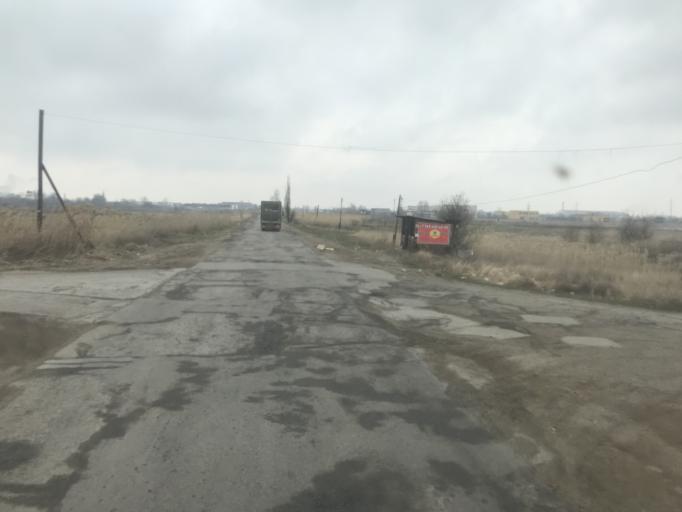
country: RU
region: Volgograd
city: Svetlyy Yar
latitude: 48.5189
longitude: 44.6265
